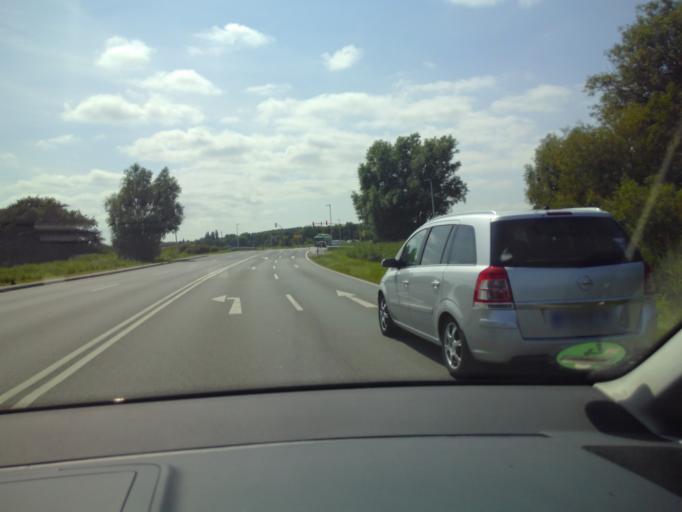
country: DE
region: Lower Saxony
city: Cuxhaven
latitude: 53.8311
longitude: 8.6792
